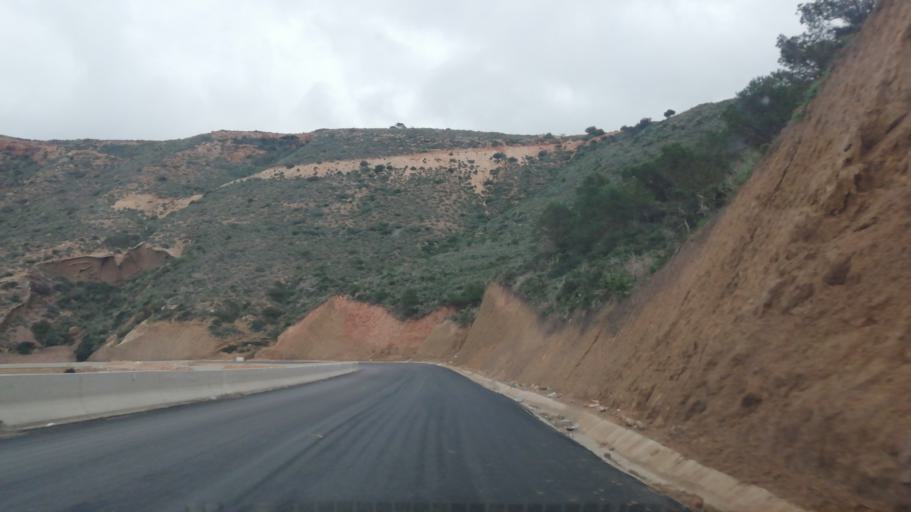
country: DZ
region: Oran
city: Bir el Djir
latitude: 35.7648
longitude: -0.5247
